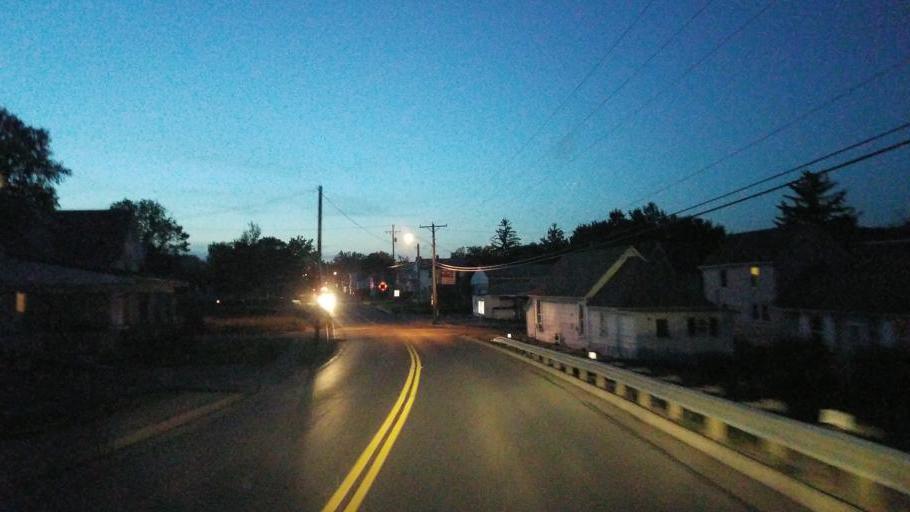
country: US
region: Ohio
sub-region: Highland County
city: Greenfield
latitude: 39.3472
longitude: -83.3900
